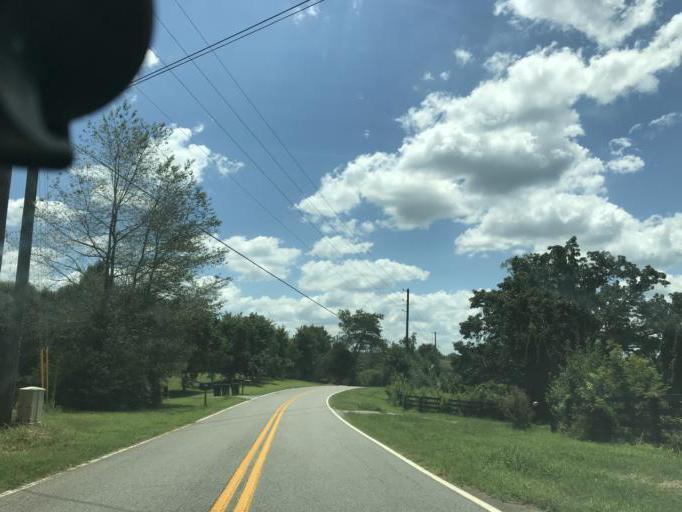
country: US
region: Georgia
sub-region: Fulton County
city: Milton
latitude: 34.2237
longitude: -84.2554
